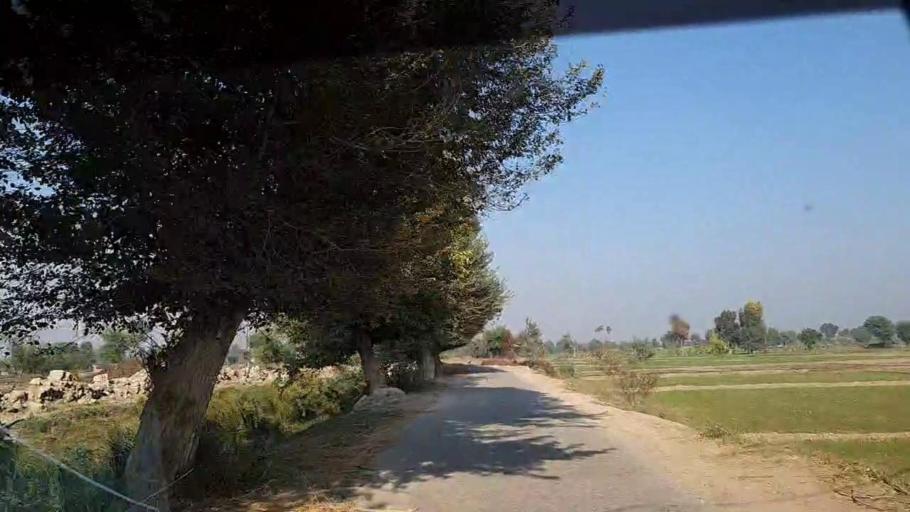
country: PK
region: Sindh
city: Sobhadero
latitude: 27.2499
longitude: 68.3282
